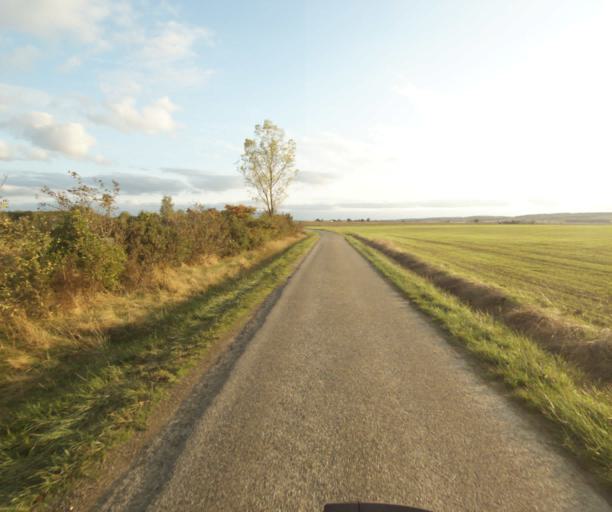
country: FR
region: Midi-Pyrenees
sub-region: Departement du Tarn-et-Garonne
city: Verdun-sur-Garonne
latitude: 43.8334
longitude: 1.1593
